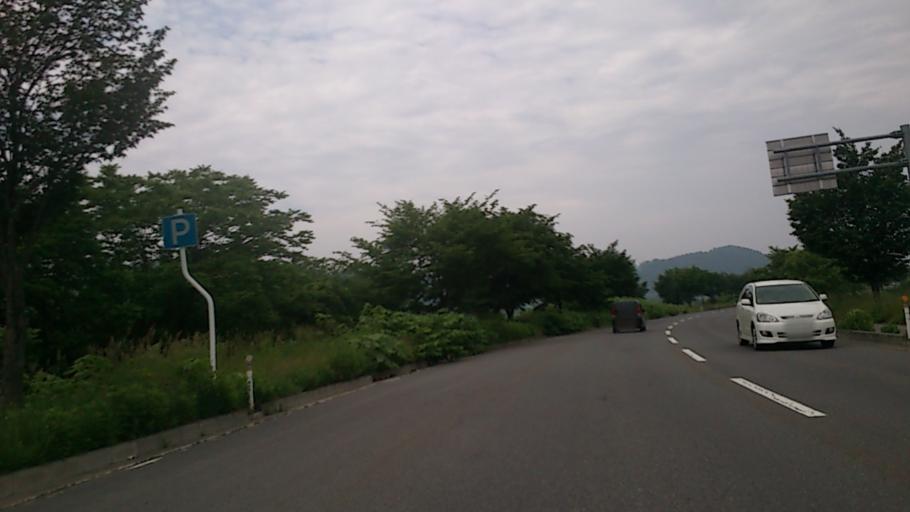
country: JP
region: Aomori
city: Hirosaki
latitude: 40.5935
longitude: 140.3557
